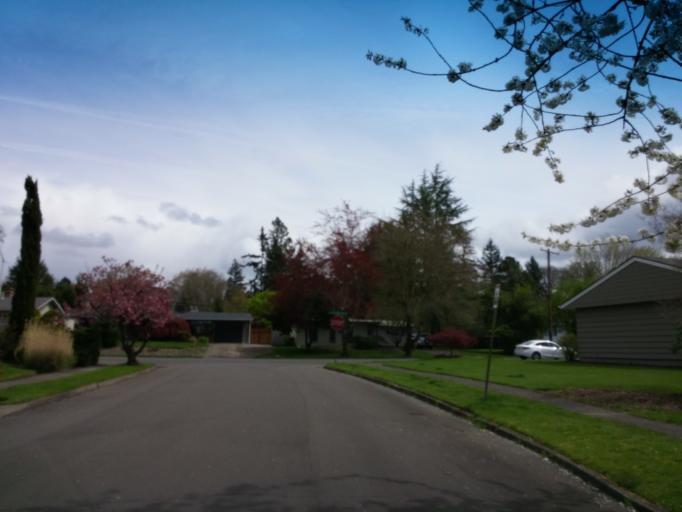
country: US
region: Oregon
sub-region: Washington County
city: Cedar Hills
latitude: 45.5074
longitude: -122.8071
